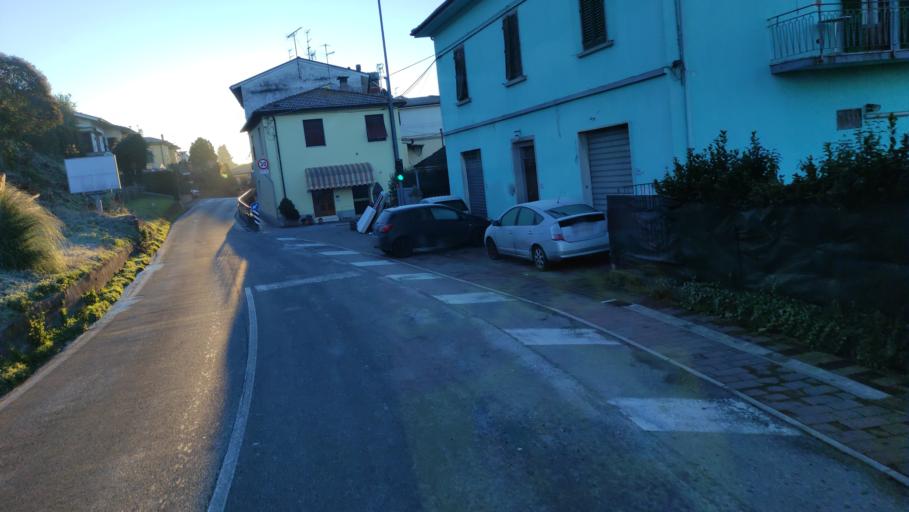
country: IT
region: Tuscany
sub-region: Province of Florence
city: Pozzale-Case Nuove
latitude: 43.6596
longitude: 10.9338
